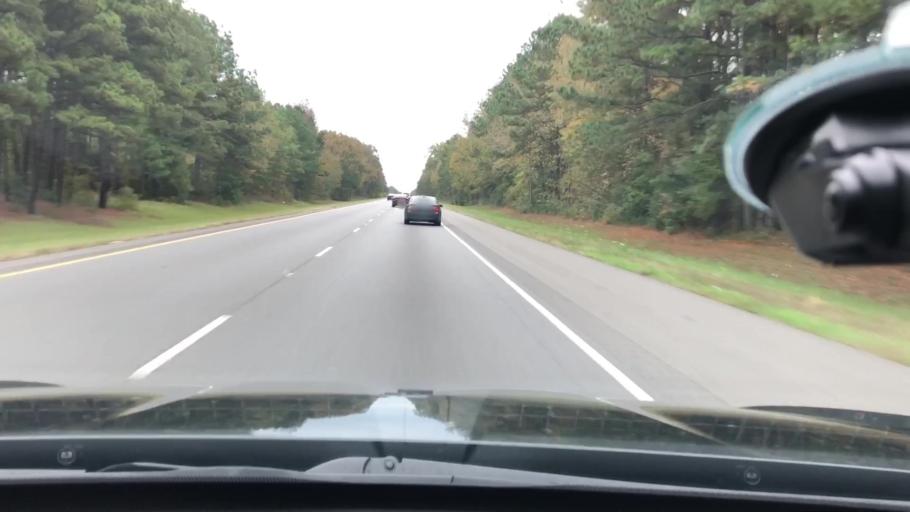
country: US
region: Arkansas
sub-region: Hempstead County
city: Hope
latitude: 33.6362
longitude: -93.7085
